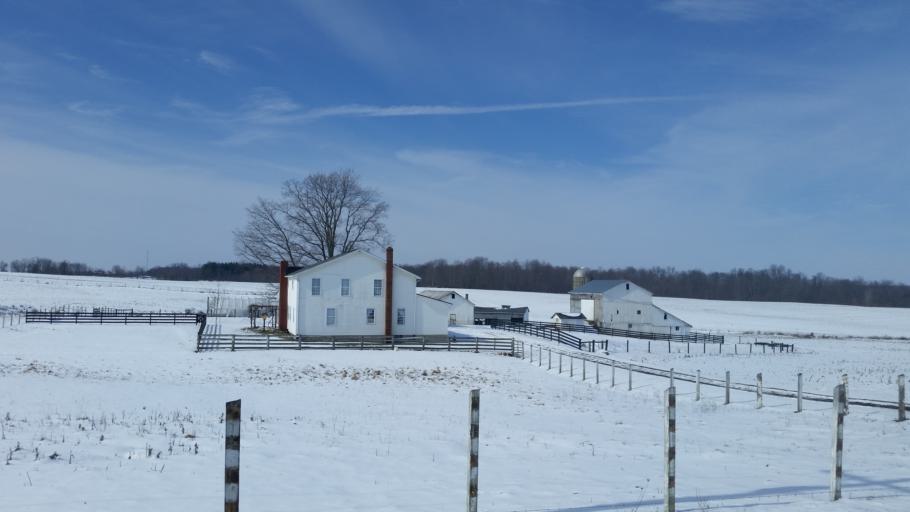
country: US
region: Ohio
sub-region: Knox County
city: Fredericktown
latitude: 40.5031
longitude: -82.6450
